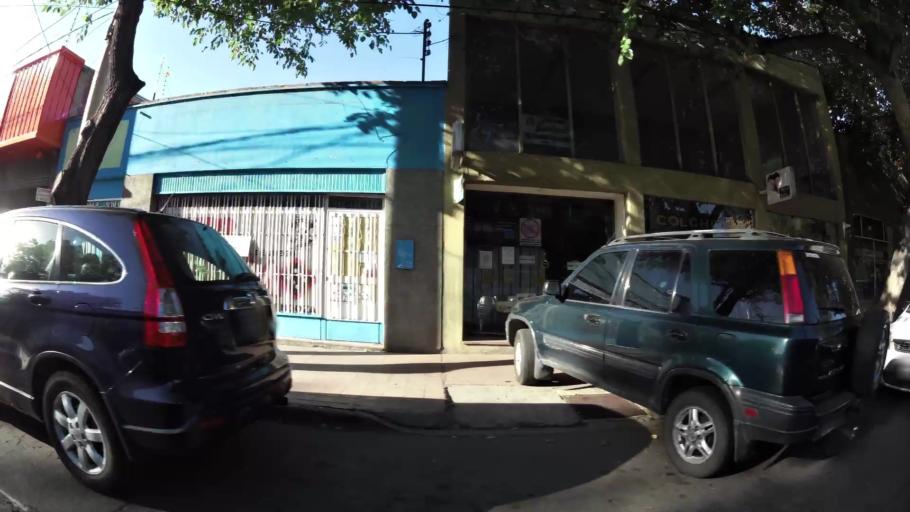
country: AR
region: Mendoza
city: Mendoza
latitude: -32.9041
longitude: -68.8415
